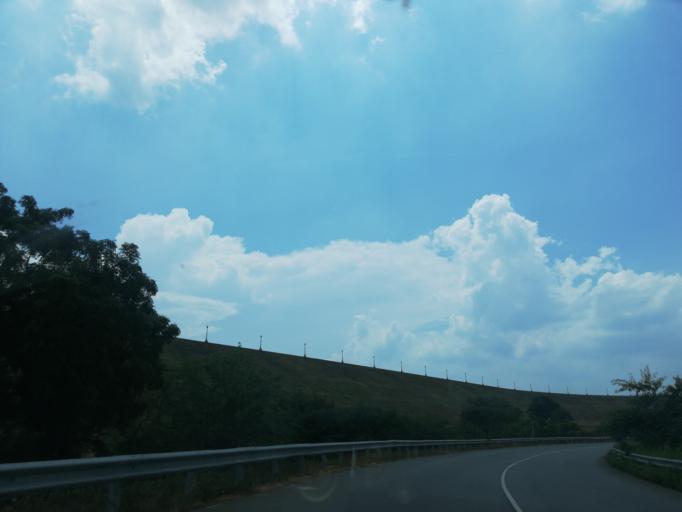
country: IN
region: Andhra Pradesh
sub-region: Guntur
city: Macherla
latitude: 16.5951
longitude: 79.3109
